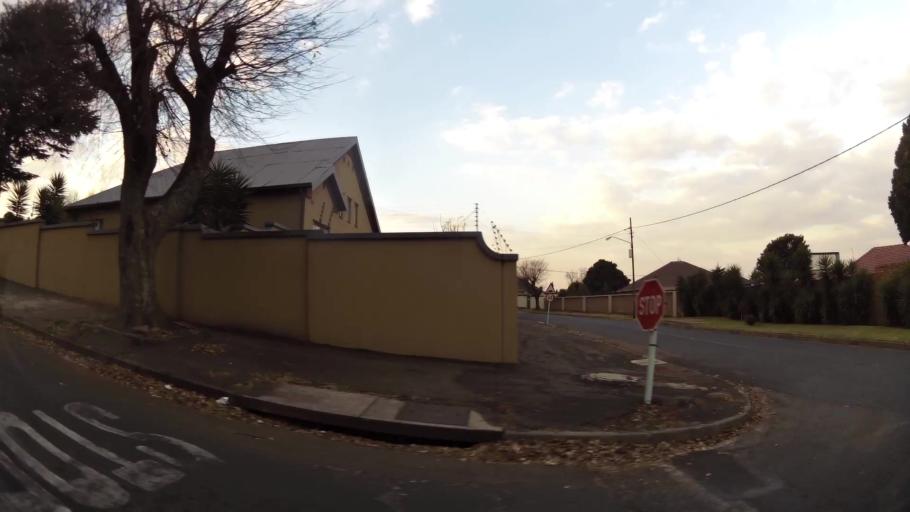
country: ZA
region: Gauteng
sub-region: Ekurhuleni Metropolitan Municipality
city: Germiston
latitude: -26.1909
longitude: 28.1499
